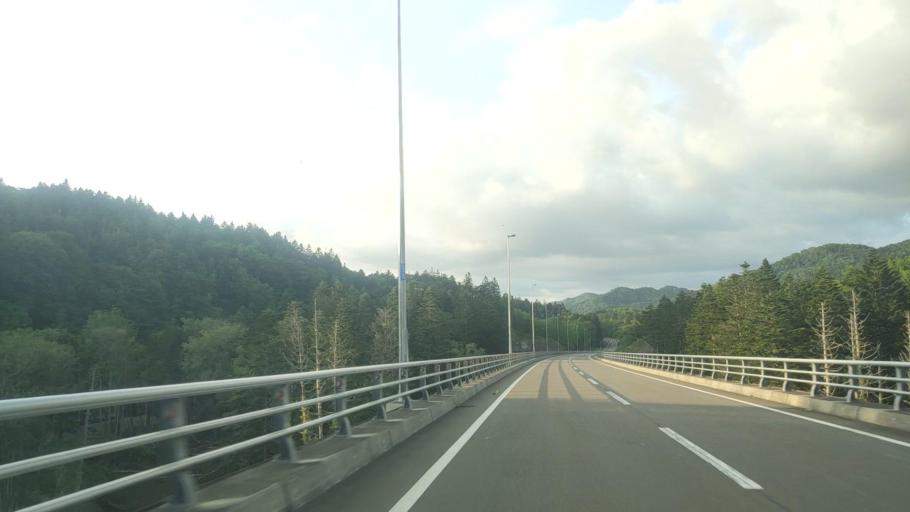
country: JP
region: Hokkaido
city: Bibai
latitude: 43.1073
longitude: 142.0981
